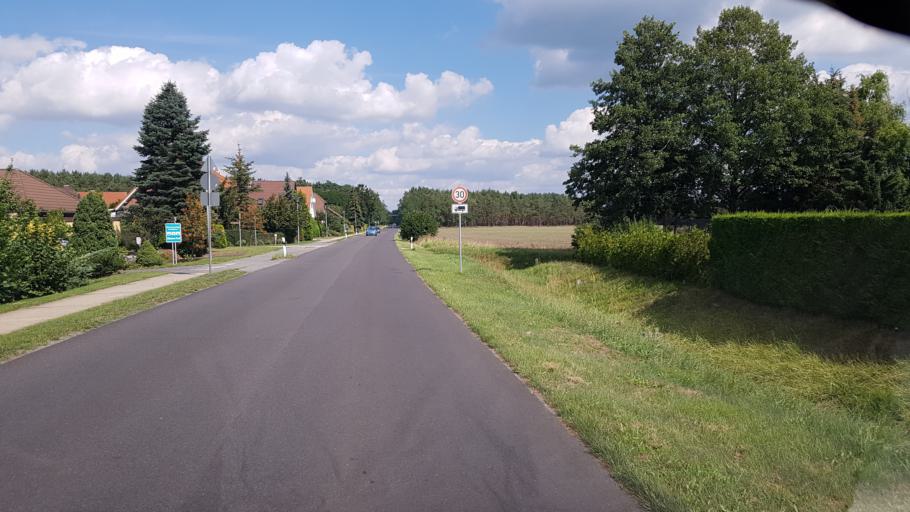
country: DE
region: Brandenburg
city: Lubbenau
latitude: 51.8464
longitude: 13.9422
